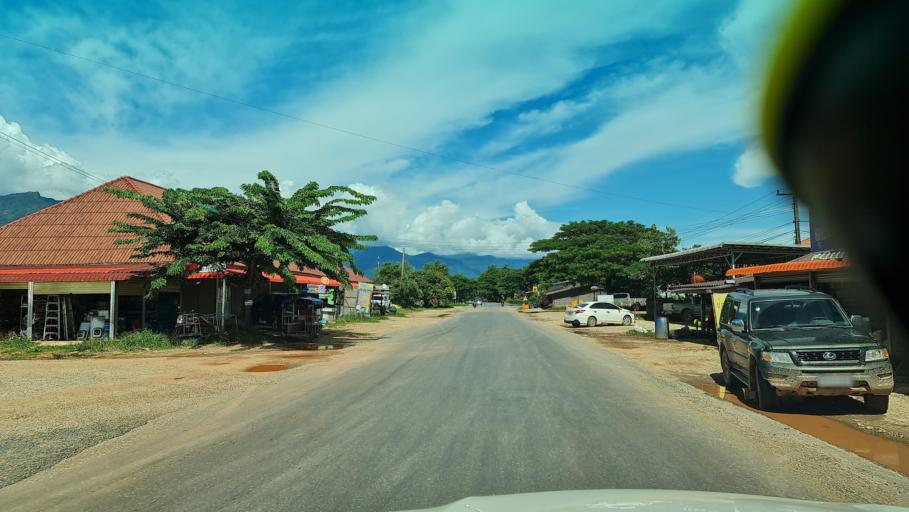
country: LA
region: Bolikhamxai
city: Ban Nahin
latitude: 18.3009
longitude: 104.1132
